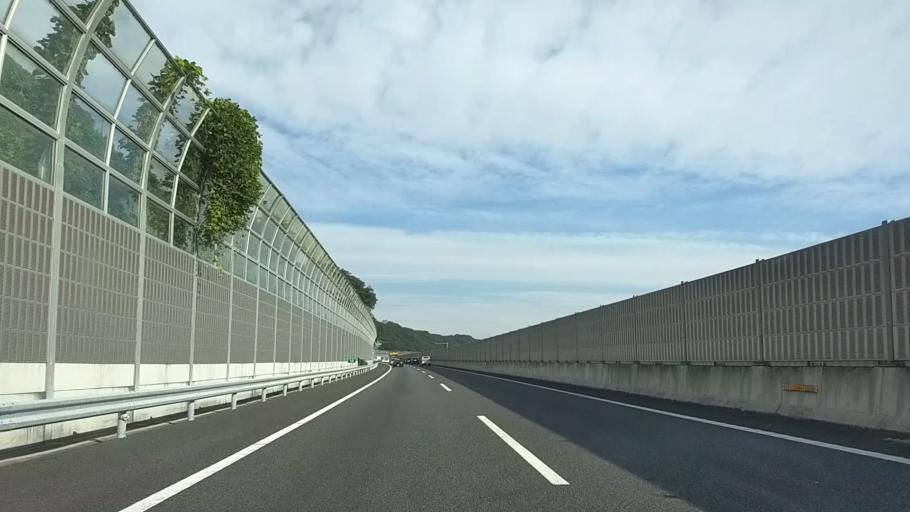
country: JP
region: Kanagawa
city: Zama
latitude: 35.4956
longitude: 139.3673
